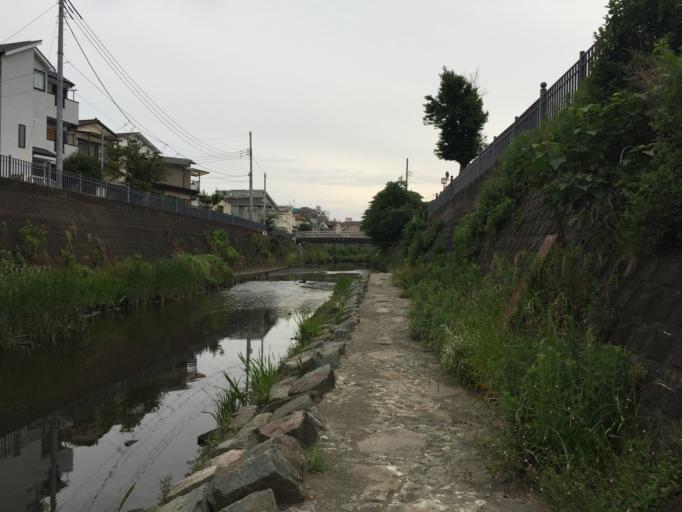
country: JP
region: Kanagawa
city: Yokohama
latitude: 35.4220
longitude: 139.5998
